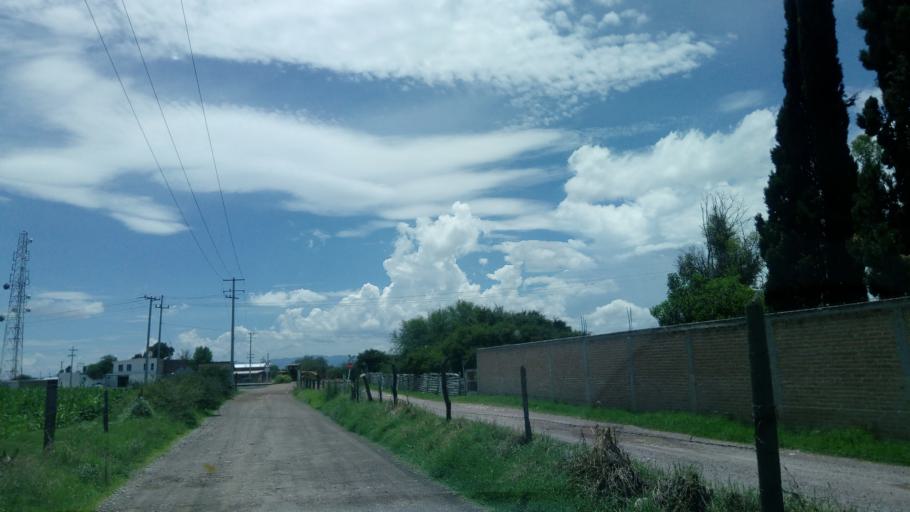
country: MX
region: Durango
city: Victoria de Durango
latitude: 24.0830
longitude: -104.5569
